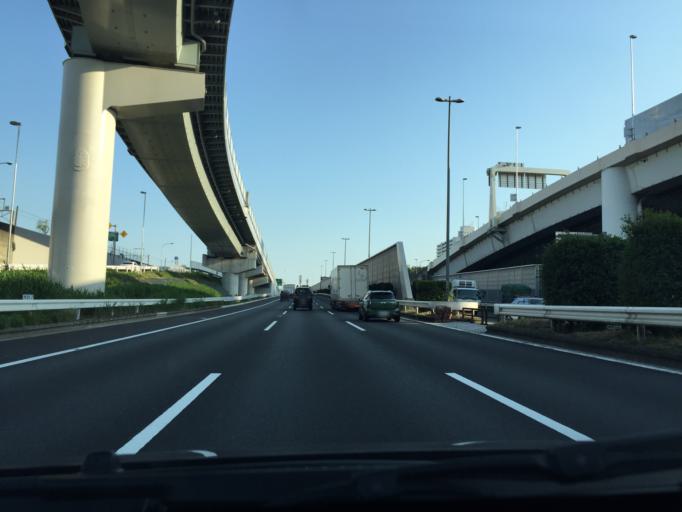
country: JP
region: Kanagawa
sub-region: Kawasaki-shi
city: Kawasaki
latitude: 35.6057
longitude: 139.7554
